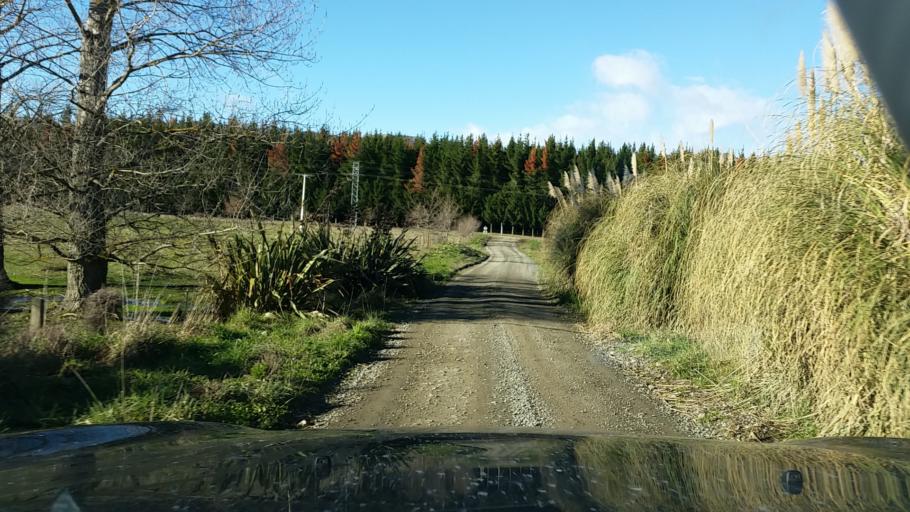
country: NZ
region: Marlborough
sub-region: Marlborough District
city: Blenheim
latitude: -41.6204
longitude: 173.6842
